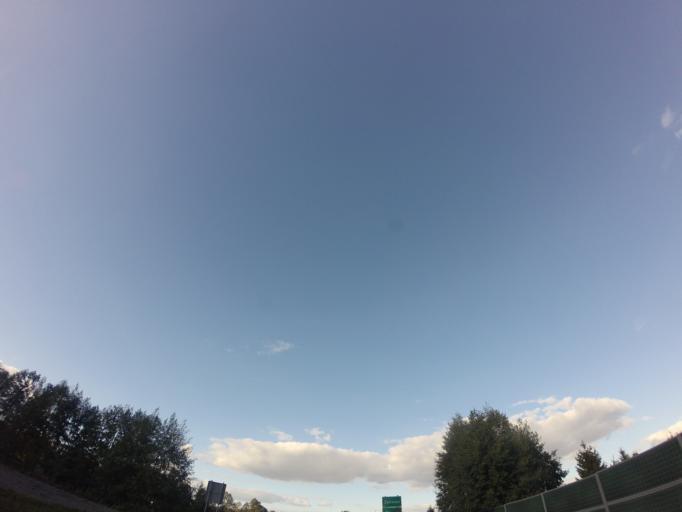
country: PL
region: Greater Poland Voivodeship
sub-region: Powiat nowotomyski
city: Nowy Tomysl
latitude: 52.3203
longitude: 16.1086
